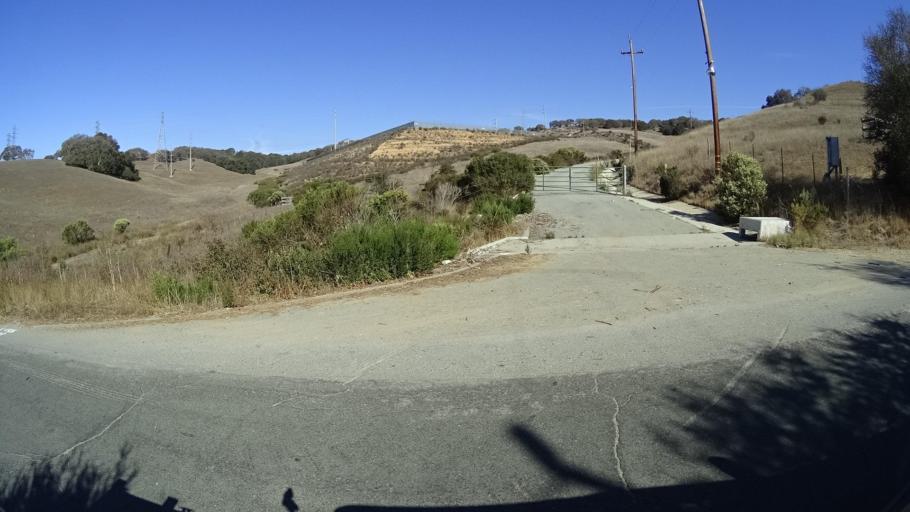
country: US
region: California
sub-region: Monterey County
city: Prunedale
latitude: 36.7775
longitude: -121.5975
